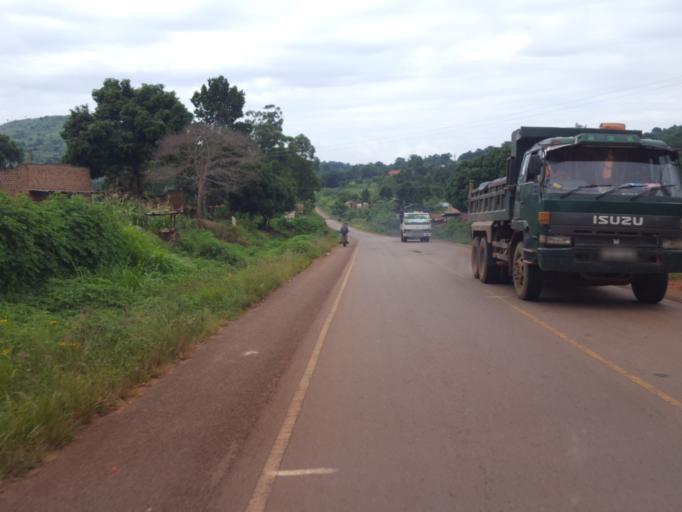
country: UG
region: Central Region
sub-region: Mityana District
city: Mityana
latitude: 0.6581
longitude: 32.0923
